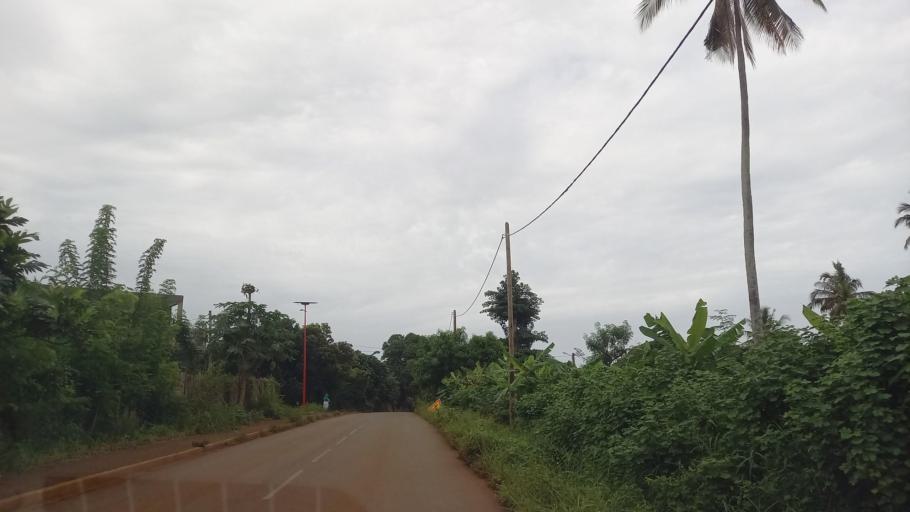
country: YT
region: Chiconi
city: Chiconi
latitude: -12.8302
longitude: 45.1264
